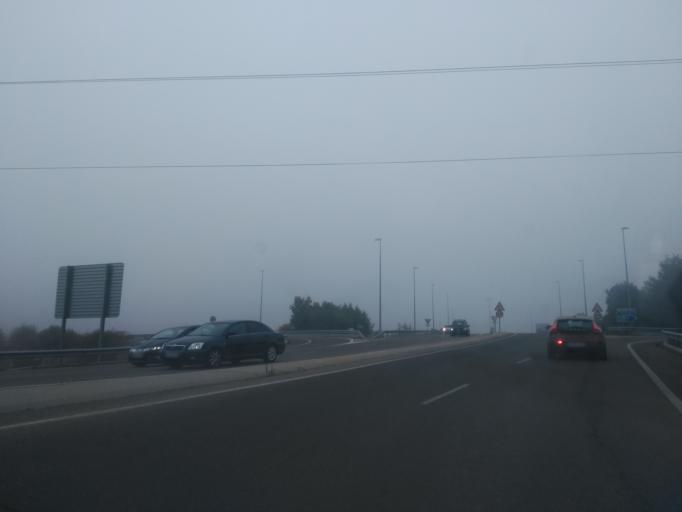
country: ES
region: Castille and Leon
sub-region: Provincia de Valladolid
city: Zaratan
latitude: 41.6343
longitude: -4.7745
